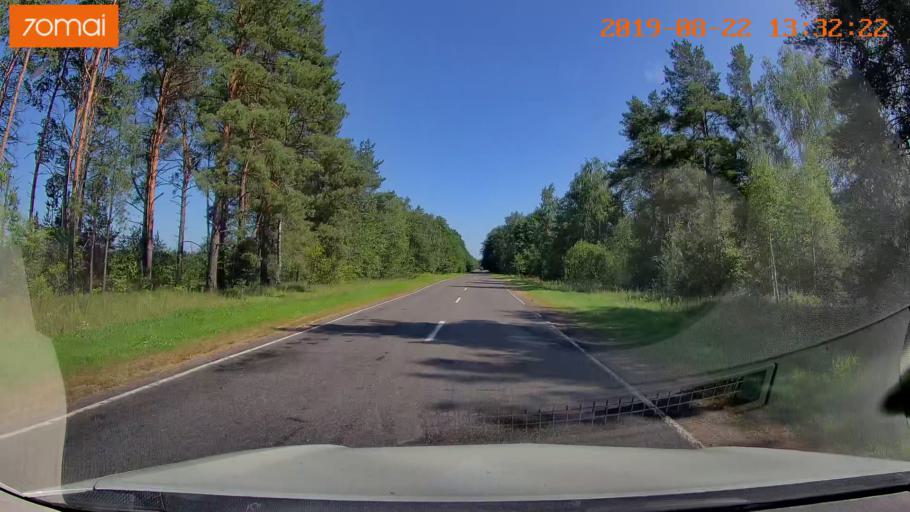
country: BY
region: Minsk
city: Staryya Darohi
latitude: 53.2171
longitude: 28.2023
